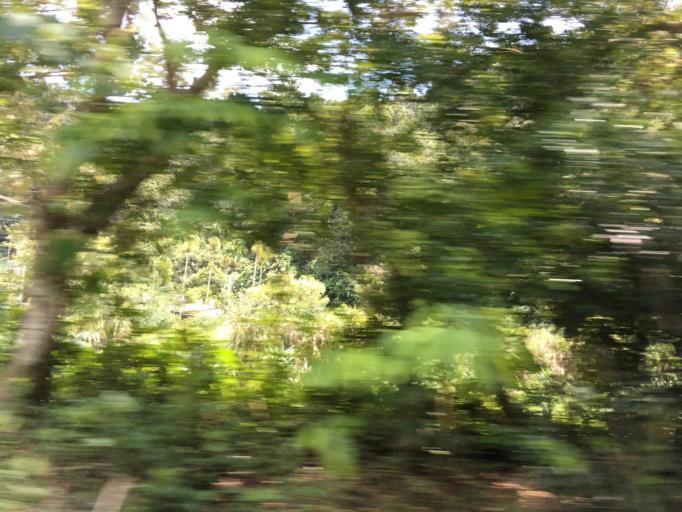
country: TW
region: Taiwan
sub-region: Yilan
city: Yilan
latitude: 24.8154
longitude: 121.7450
